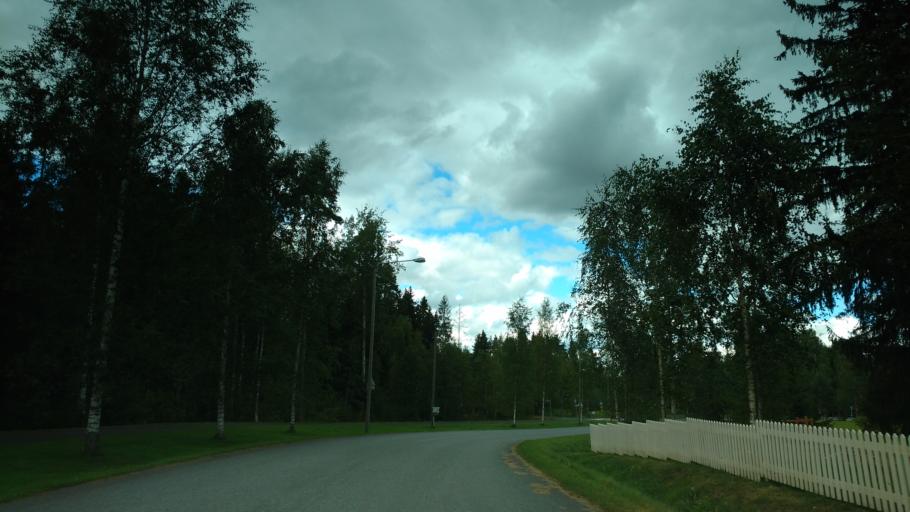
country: FI
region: Haeme
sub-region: Forssa
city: Ypaejae
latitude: 60.8098
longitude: 23.2623
